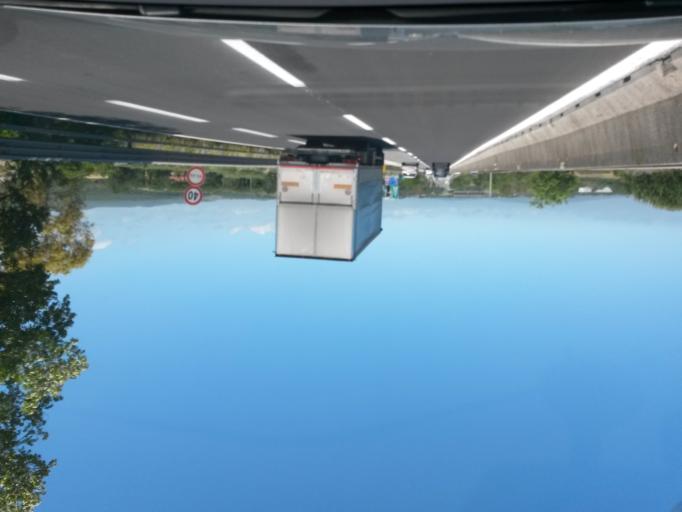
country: IT
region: Tuscany
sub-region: Provincia di Livorno
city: Cecina
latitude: 43.3176
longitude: 10.5341
